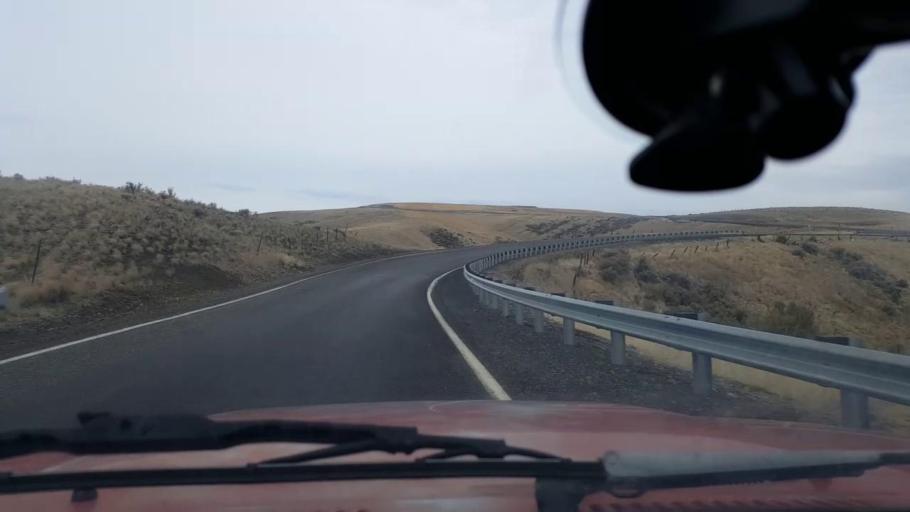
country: US
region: Washington
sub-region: Asotin County
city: Clarkston Heights-Vineland
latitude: 46.3330
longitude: -117.2965
